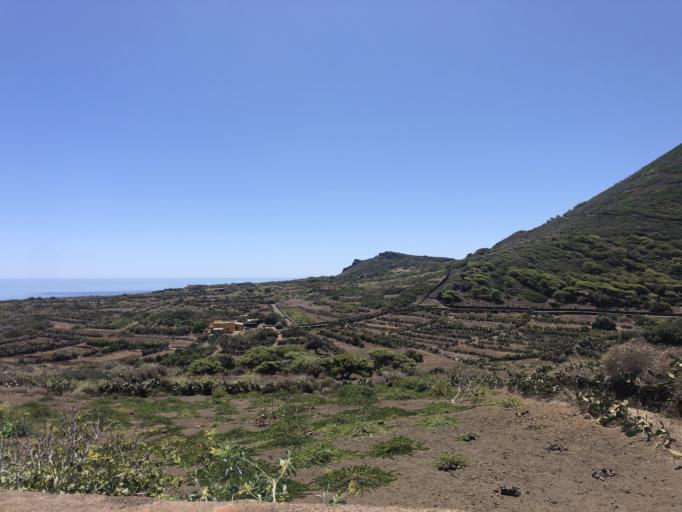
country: IT
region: Sicily
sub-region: Agrigento
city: Lampedusa
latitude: 35.8647
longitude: 12.8752
